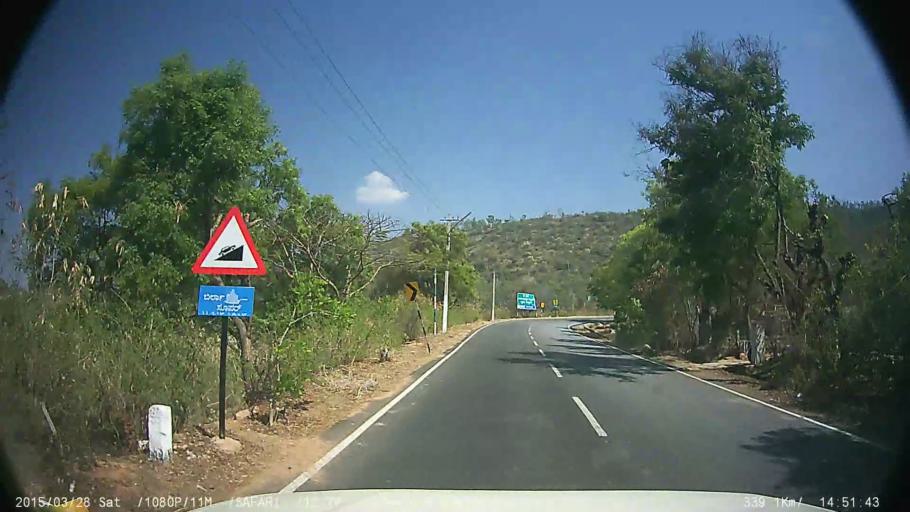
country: IN
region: Karnataka
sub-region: Mysore
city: Mysore
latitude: 12.2875
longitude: 76.6863
